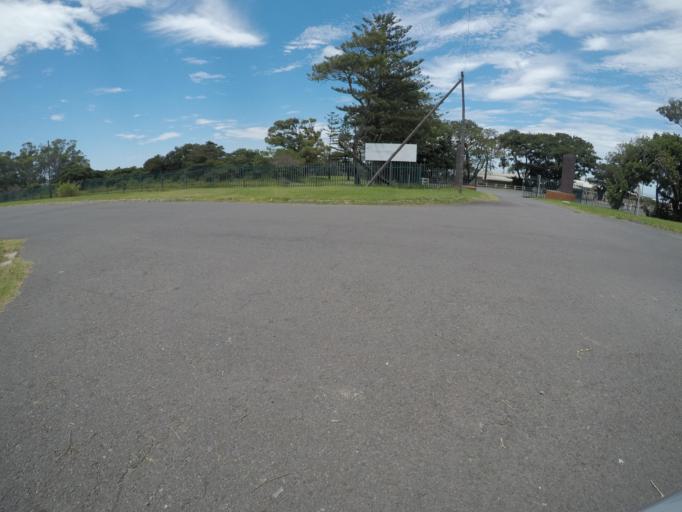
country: ZA
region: Eastern Cape
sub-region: Buffalo City Metropolitan Municipality
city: East London
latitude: -33.0423
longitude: 27.8567
